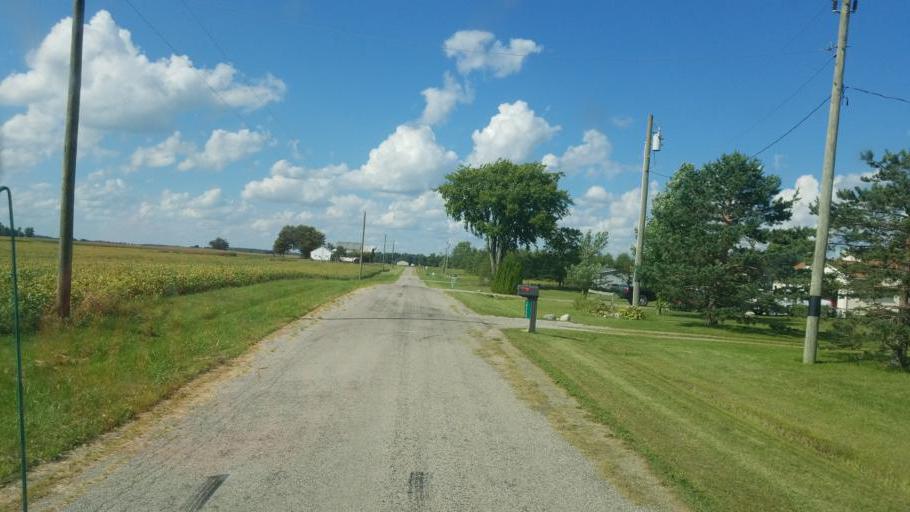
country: US
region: Ohio
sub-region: Union County
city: Richwood
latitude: 40.5023
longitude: -83.3682
